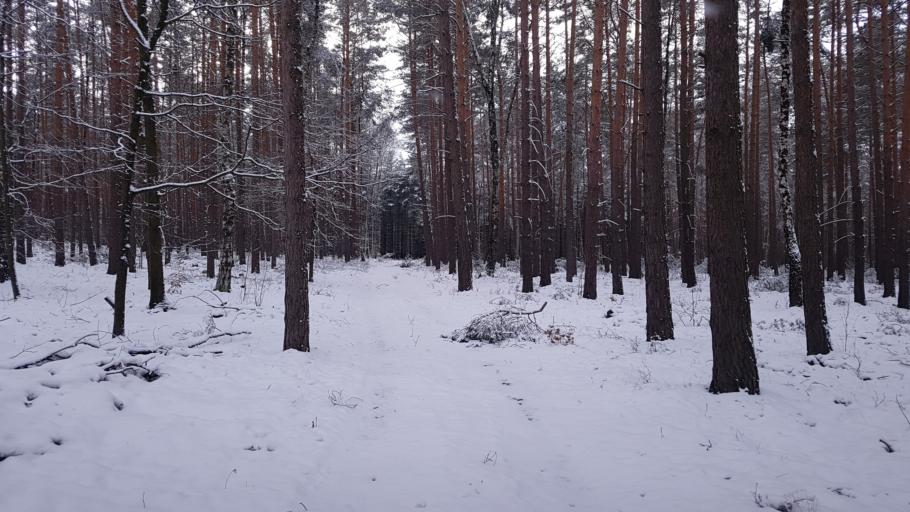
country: DE
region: Brandenburg
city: Crinitz
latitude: 51.7323
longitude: 13.7769
